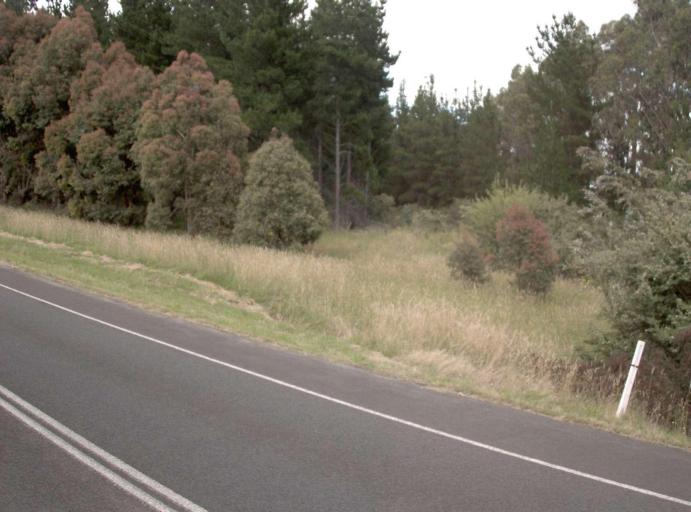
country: AU
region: Victoria
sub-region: Latrobe
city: Morwell
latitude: -38.1920
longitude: 146.4505
